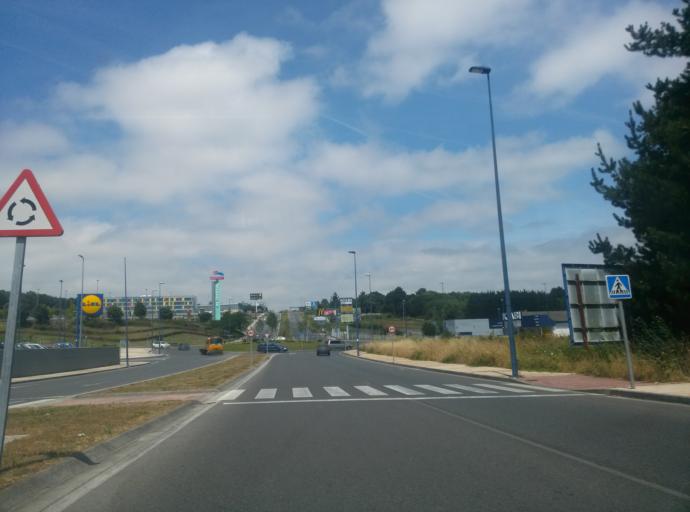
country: ES
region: Galicia
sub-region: Provincia de Lugo
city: Lugo
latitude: 43.0356
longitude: -7.5651
